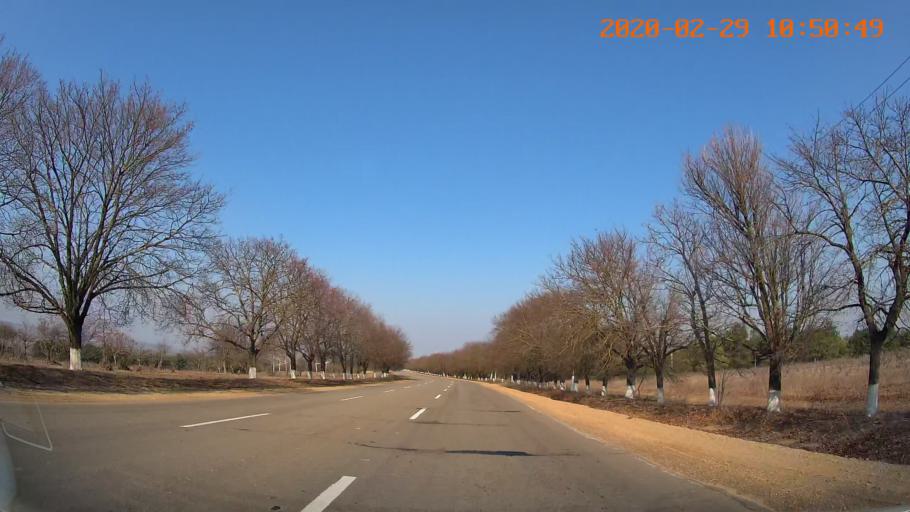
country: MD
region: Telenesti
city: Grigoriopol
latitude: 47.0869
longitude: 29.3718
